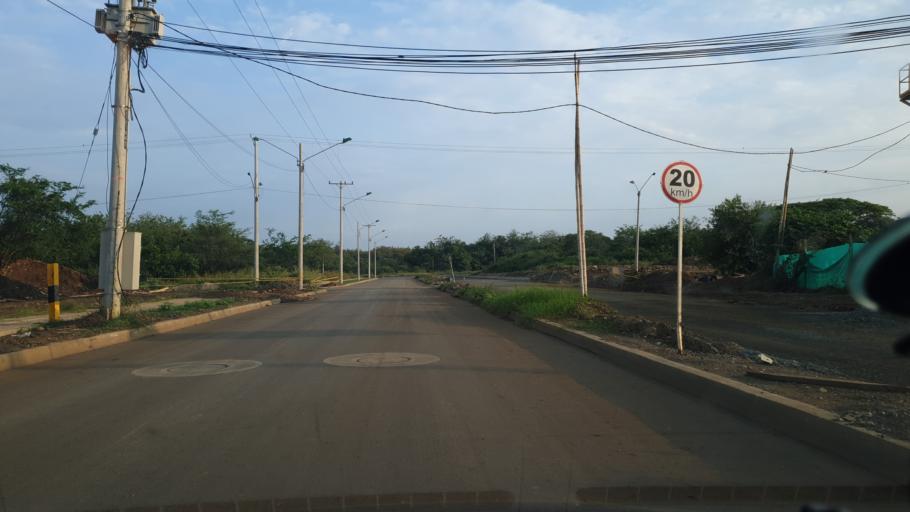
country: CO
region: Valle del Cauca
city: Jamundi
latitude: 3.3450
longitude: -76.5209
